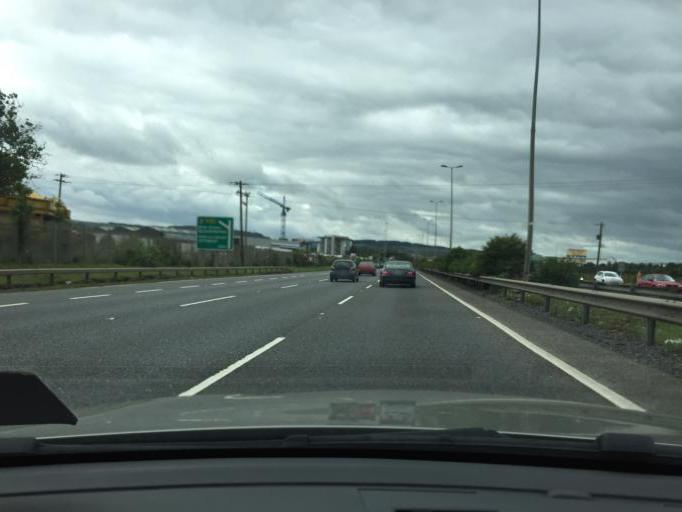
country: IE
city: Jobstown
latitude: 53.2989
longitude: -6.4236
